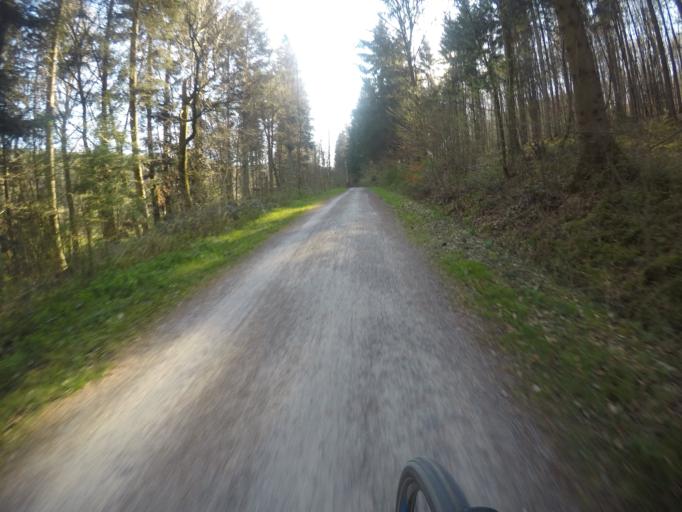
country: DE
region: Baden-Wuerttemberg
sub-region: Regierungsbezirk Stuttgart
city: Waldenbuch
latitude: 48.6332
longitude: 9.1751
